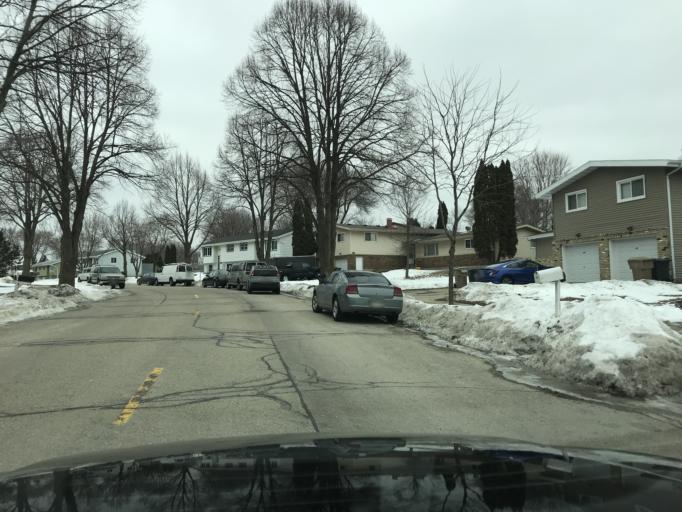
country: US
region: Wisconsin
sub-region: Dane County
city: Monona
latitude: 43.0811
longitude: -89.2839
